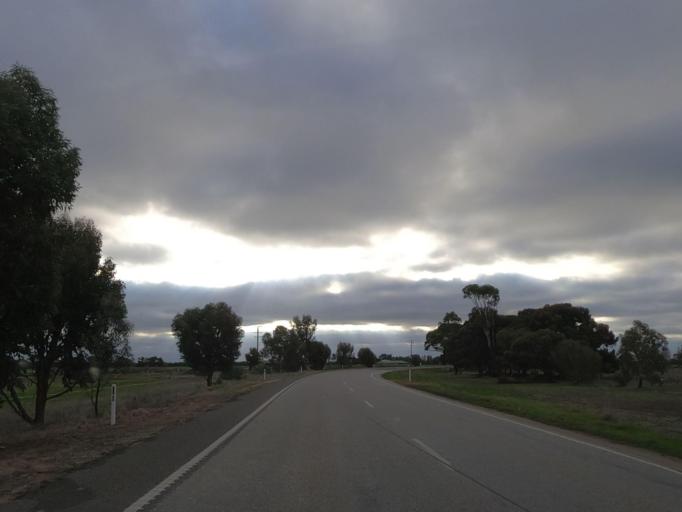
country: AU
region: Victoria
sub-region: Swan Hill
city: Swan Hill
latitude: -35.7297
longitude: 143.8932
